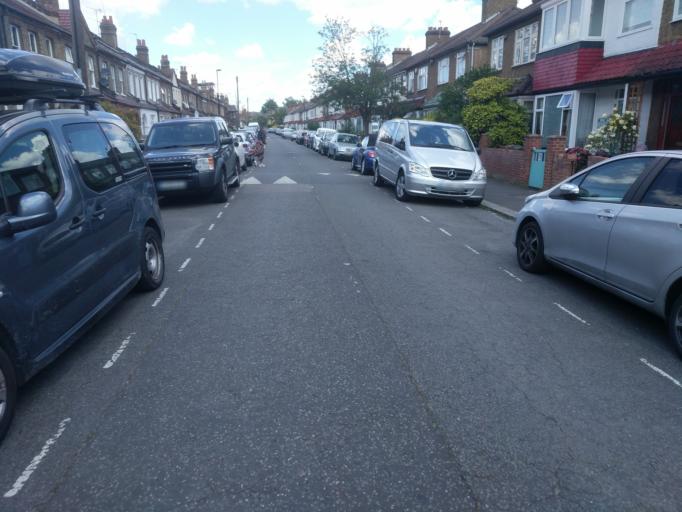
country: GB
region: England
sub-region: Greater London
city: Catford
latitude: 51.4539
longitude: -0.0214
